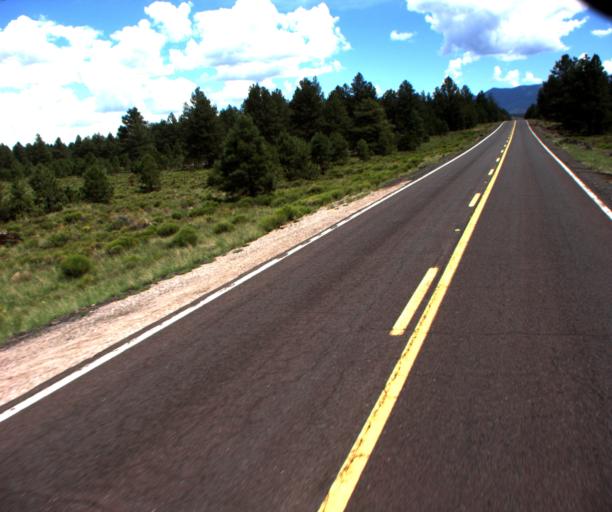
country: US
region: Arizona
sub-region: Coconino County
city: Parks
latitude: 35.4715
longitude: -111.7905
